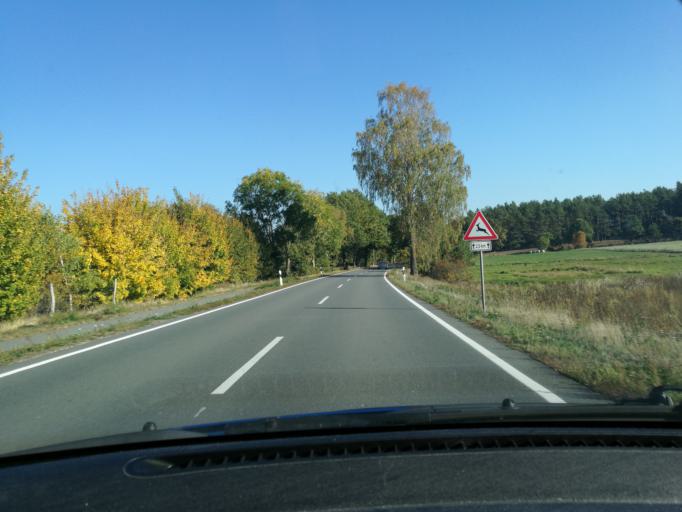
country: DE
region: Lower Saxony
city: Gohrde
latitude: 53.1506
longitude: 10.8456
